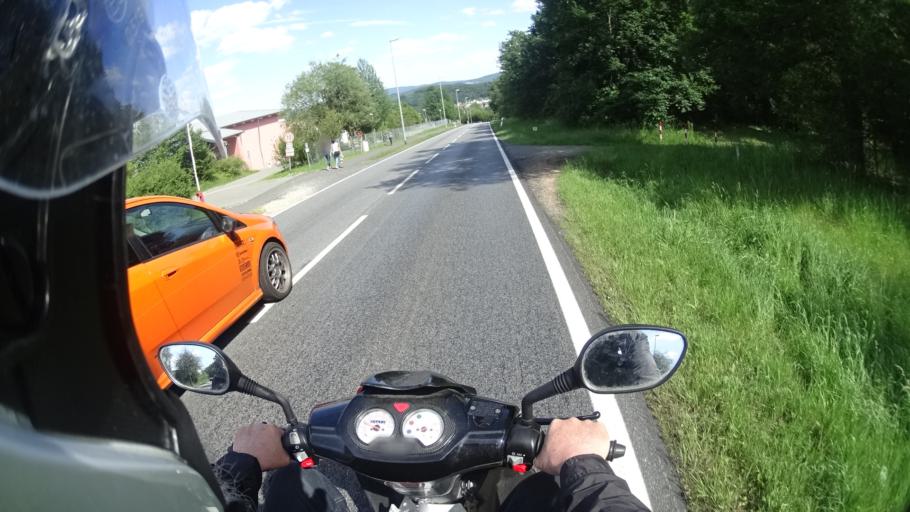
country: DE
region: Hesse
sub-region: Regierungsbezirk Darmstadt
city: Bad Schwalbach
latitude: 50.1411
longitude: 8.0531
